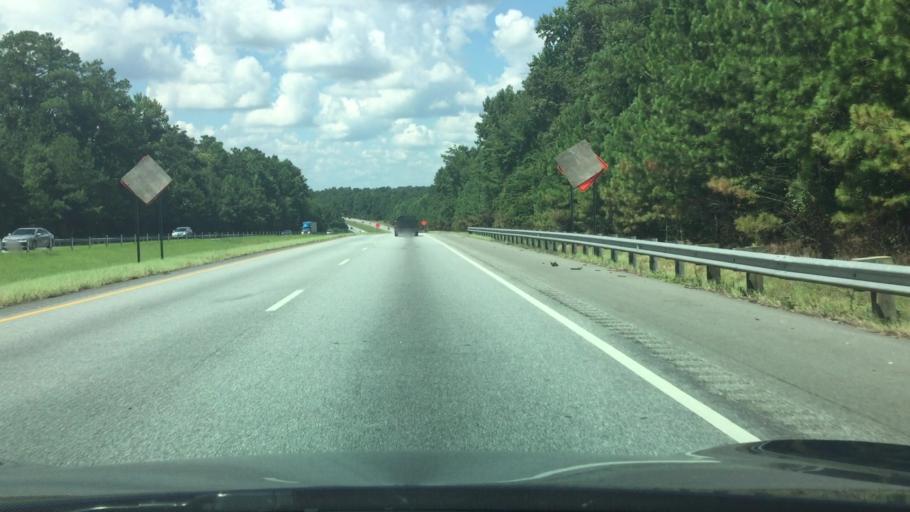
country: US
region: Alabama
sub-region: Lee County
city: Auburn
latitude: 32.5984
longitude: -85.4438
